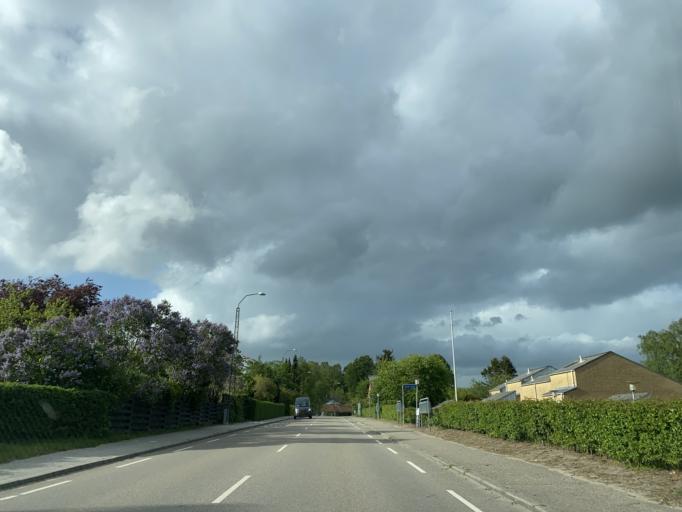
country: DK
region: Central Jutland
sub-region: Skanderborg Kommune
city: Ry
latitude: 56.0707
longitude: 9.6961
